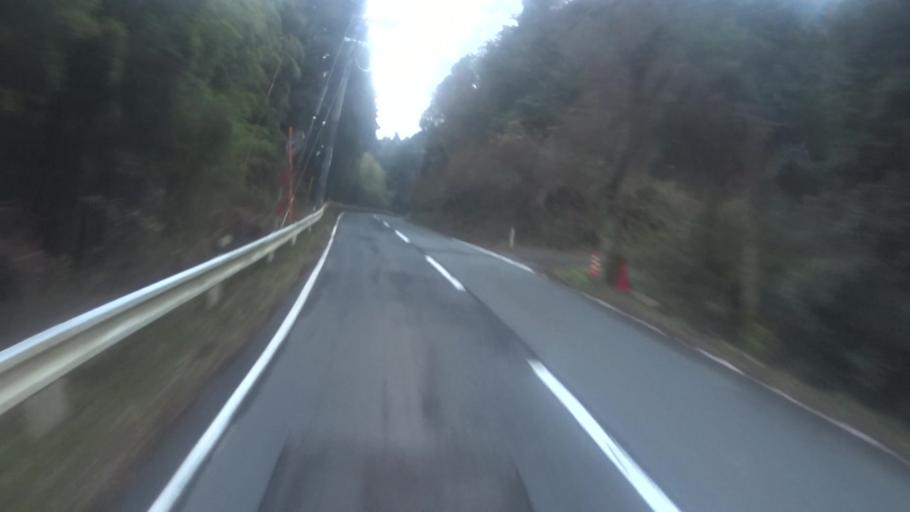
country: JP
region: Kyoto
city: Ayabe
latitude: 35.3157
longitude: 135.3168
